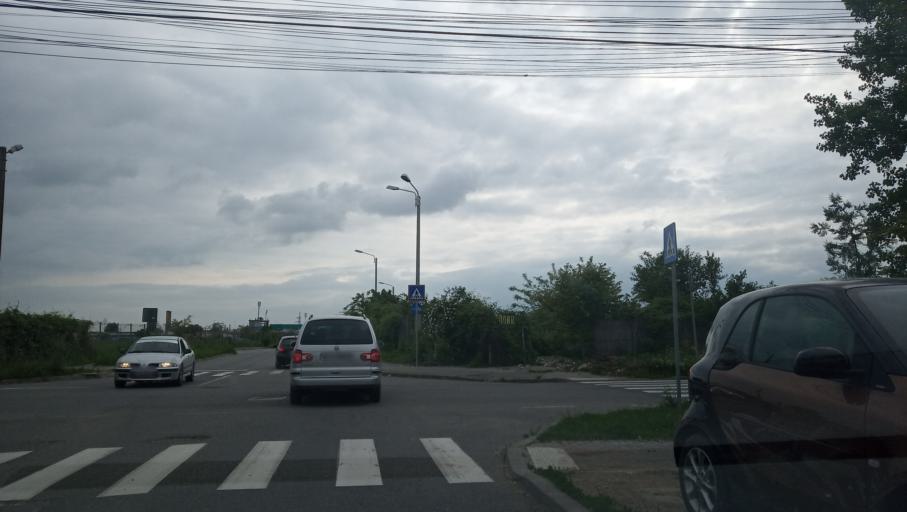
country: RO
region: Timis
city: Timisoara
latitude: 45.7475
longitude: 21.2591
